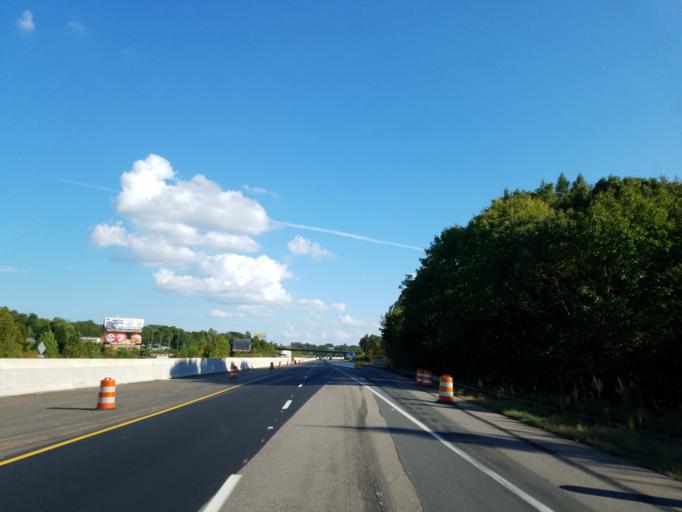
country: US
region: North Carolina
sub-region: Rowan County
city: Landis
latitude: 35.5126
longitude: -80.5672
